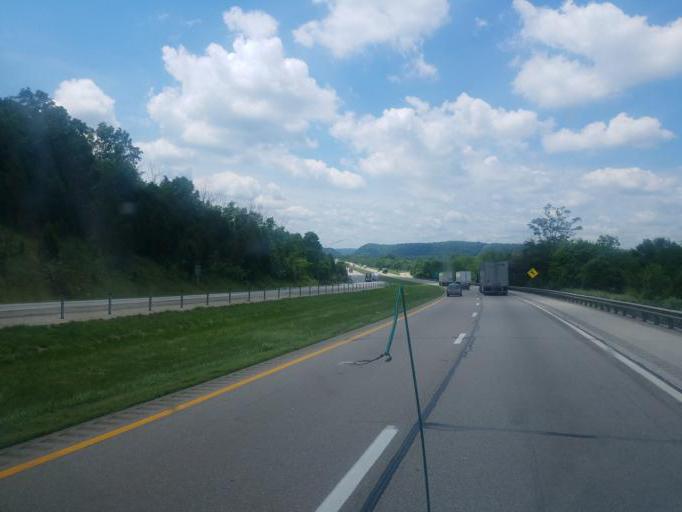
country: US
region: Kentucky
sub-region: Carroll County
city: Carrollton
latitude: 38.6532
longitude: -85.1137
